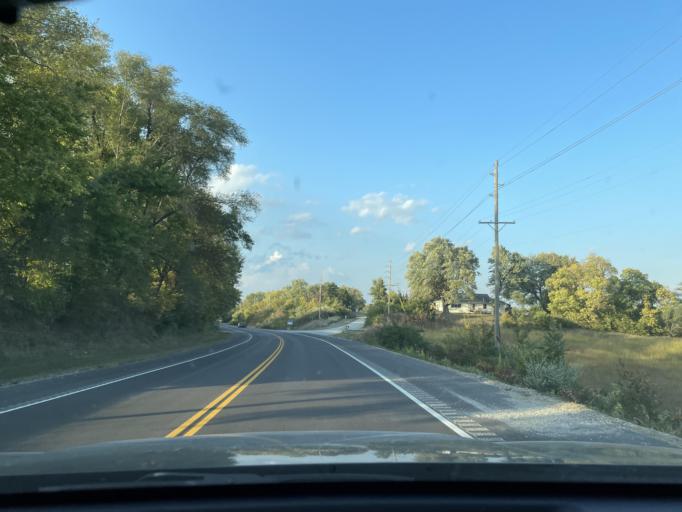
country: US
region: Missouri
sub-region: Andrew County
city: Country Club Village
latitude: 39.8472
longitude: -94.8695
